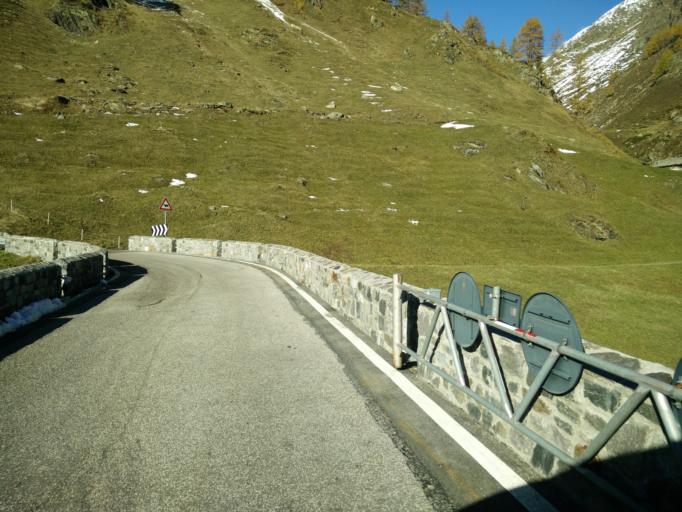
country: IT
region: Trentino-Alto Adige
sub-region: Bolzano
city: Moso in Passiria
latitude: 46.8964
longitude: 11.1298
